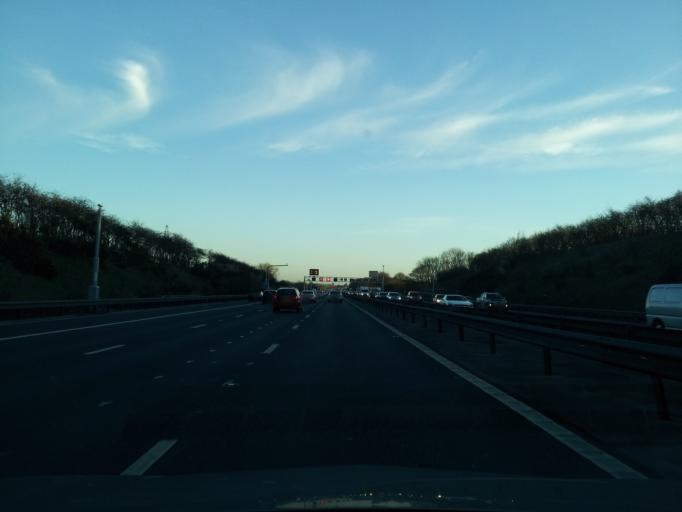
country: GB
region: England
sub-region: Central Bedfordshire
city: Steppingley
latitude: 51.9930
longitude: -0.5365
